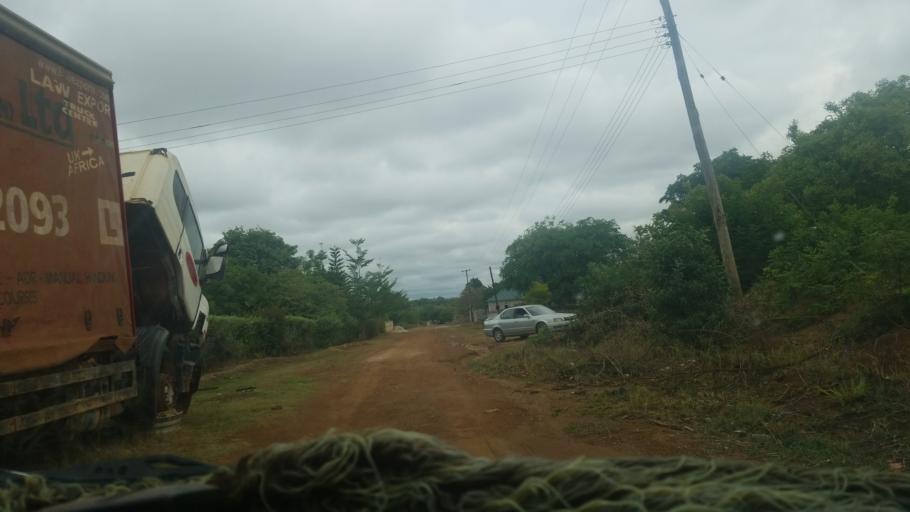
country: ZM
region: Luapula
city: Mansa
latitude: -11.1947
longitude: 28.9015
